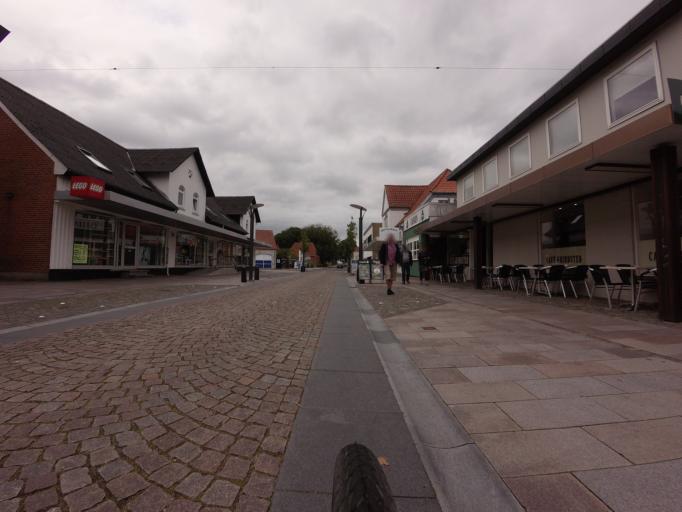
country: DK
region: South Denmark
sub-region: Billund Kommune
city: Grindsted
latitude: 55.7574
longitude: 8.9265
